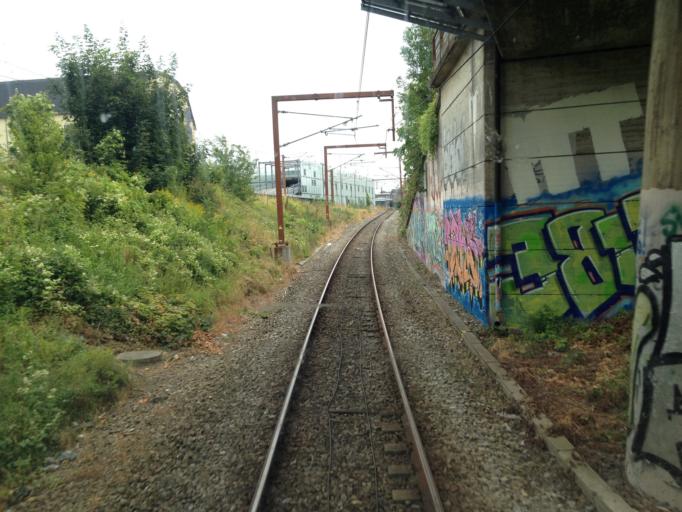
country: DK
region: Capital Region
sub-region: Kobenhavn
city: Vanlose
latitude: 55.6642
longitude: 12.5087
